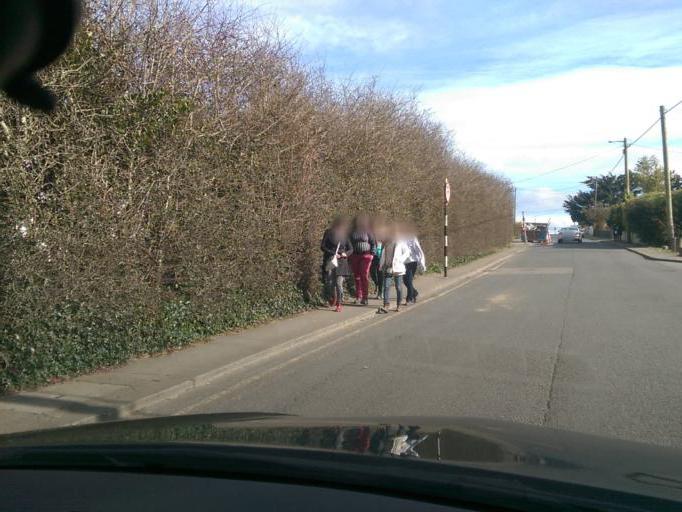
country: IE
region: Leinster
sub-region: Fingal County
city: Howth
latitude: 53.3721
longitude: -6.0576
